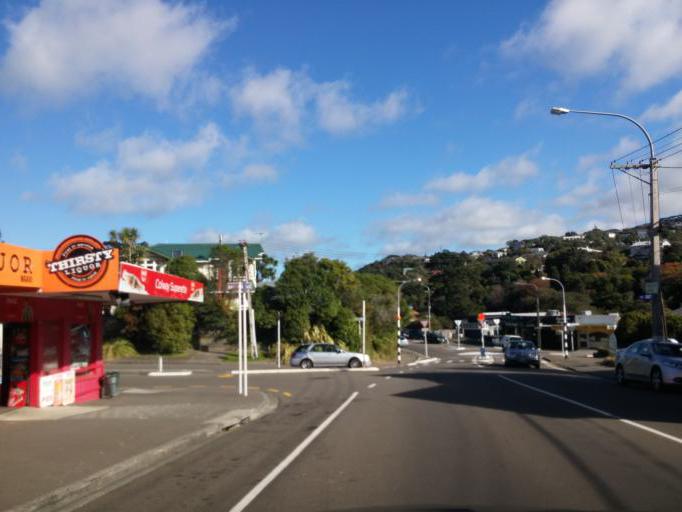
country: NZ
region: Wellington
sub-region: Wellington City
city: Kelburn
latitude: -41.2473
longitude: 174.7754
